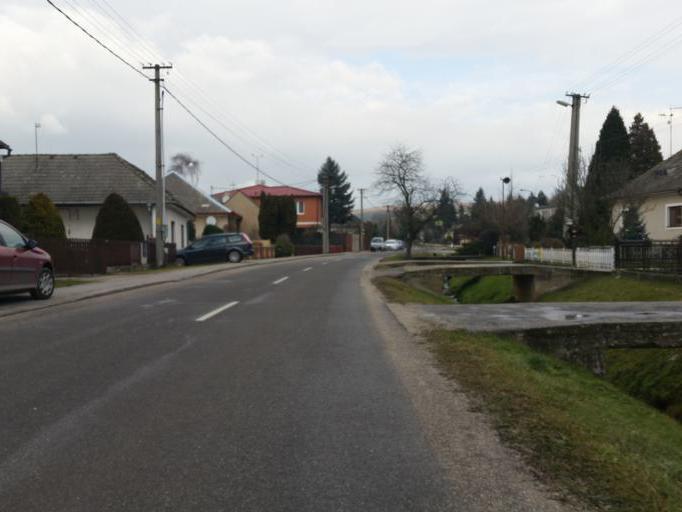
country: SK
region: Trnavsky
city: Vrbove
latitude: 48.6539
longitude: 17.7175
